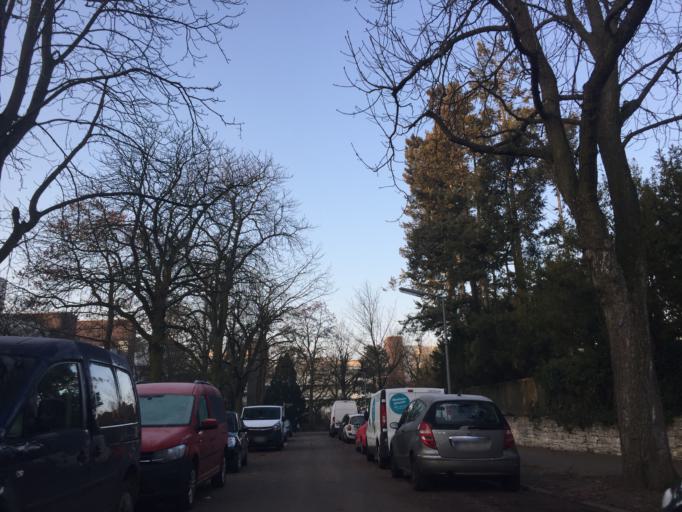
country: DE
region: Berlin
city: Gatow
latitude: 52.5033
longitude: 13.2153
